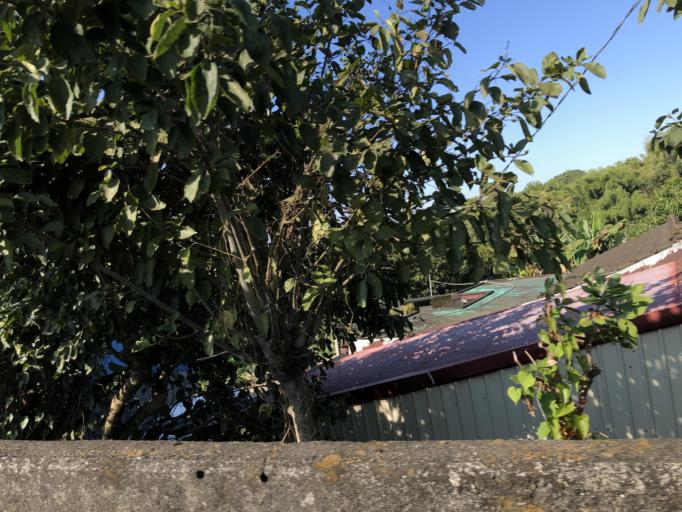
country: TW
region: Taiwan
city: Yujing
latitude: 23.0309
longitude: 120.3838
